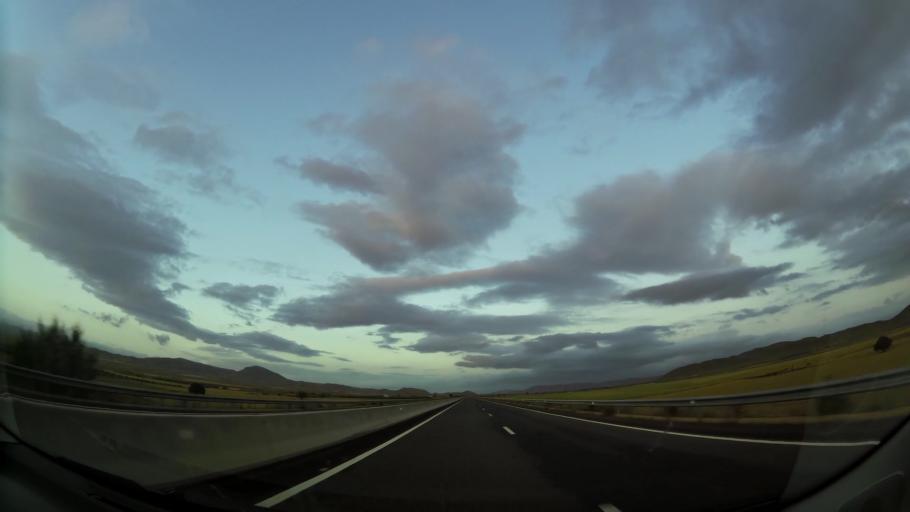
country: MA
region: Oriental
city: El Aioun
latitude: 34.5978
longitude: -2.7230
